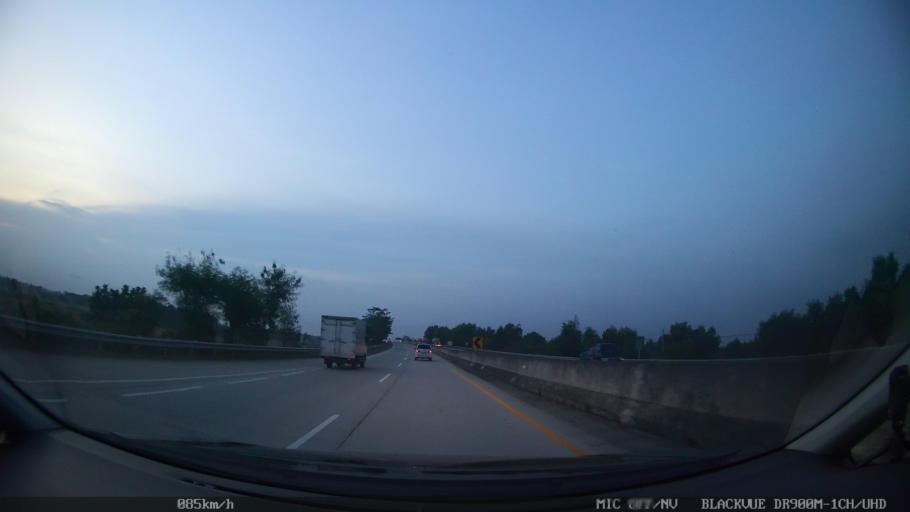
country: ID
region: Lampung
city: Sidorejo
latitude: -5.6041
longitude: 105.5550
